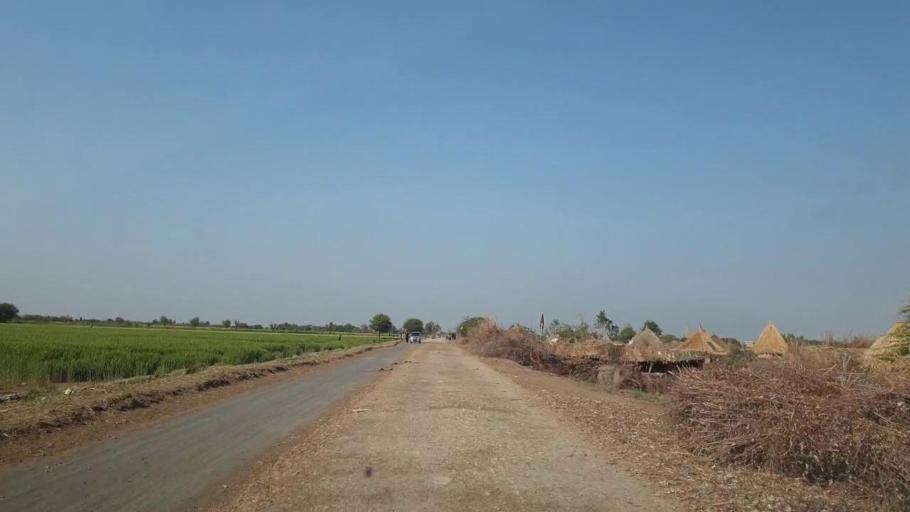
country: PK
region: Sindh
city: Tando Mittha Khan
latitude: 25.7616
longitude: 69.1937
